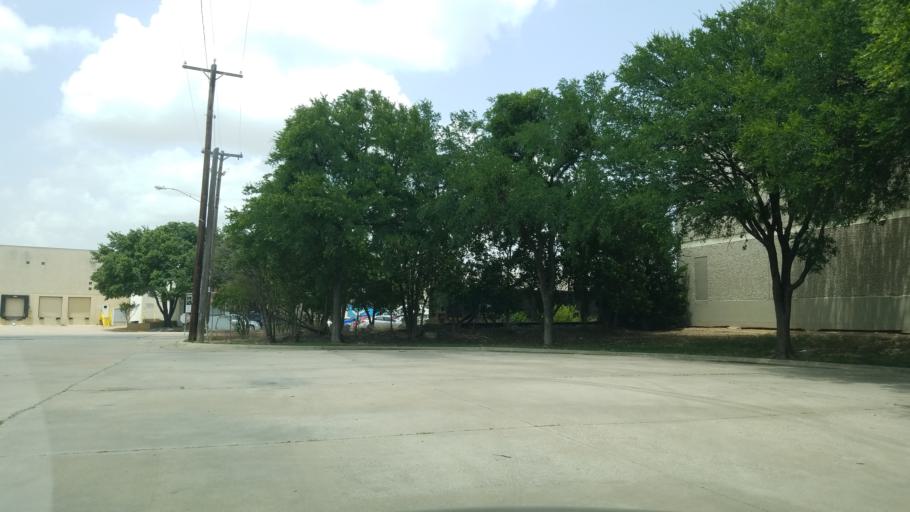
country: US
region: Texas
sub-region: Dallas County
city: Cockrell Hill
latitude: 32.7717
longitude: -96.8890
